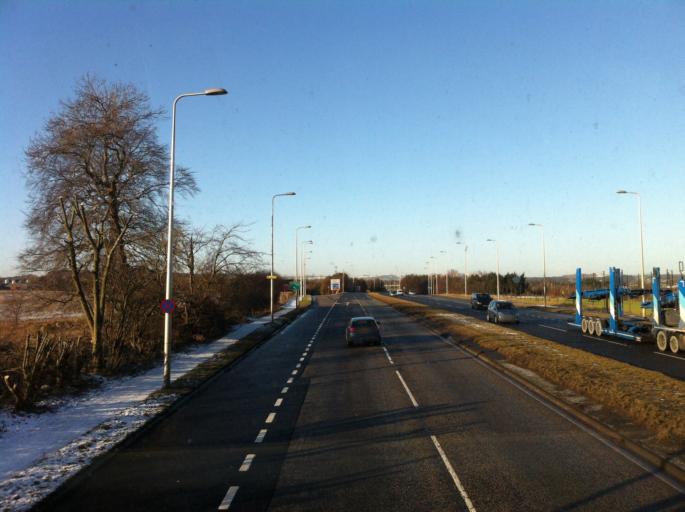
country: GB
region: Scotland
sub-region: Edinburgh
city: Ratho
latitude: 55.9367
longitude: -3.3519
